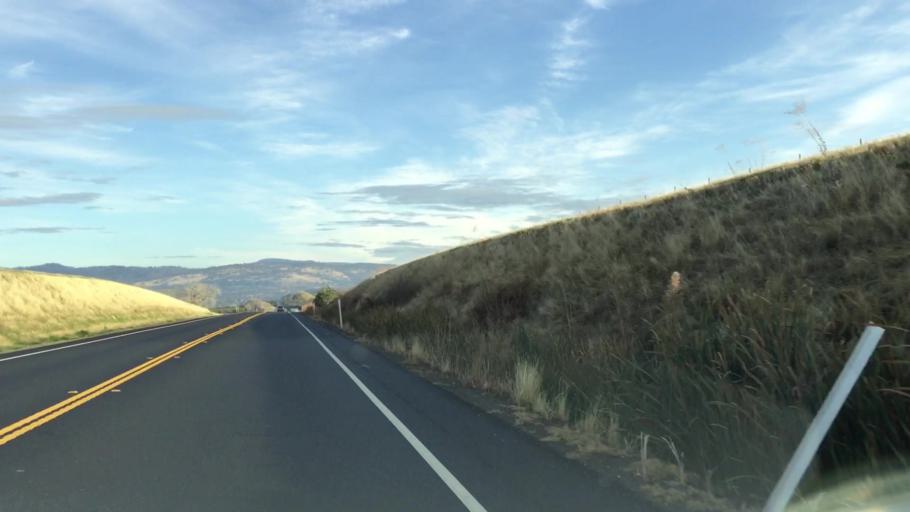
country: US
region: California
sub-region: Butte County
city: Thermalito
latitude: 39.6190
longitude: -121.6002
